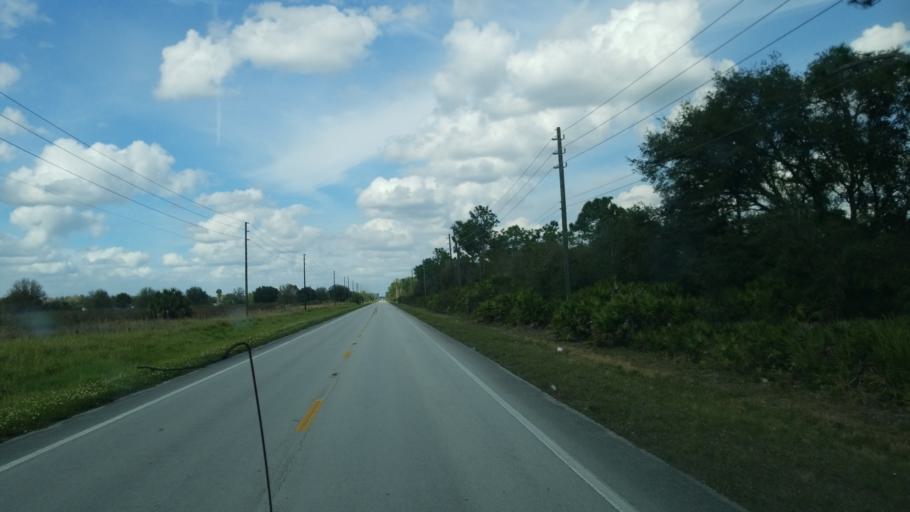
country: US
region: Florida
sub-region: Osceola County
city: Saint Cloud
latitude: 28.1120
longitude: -81.0763
